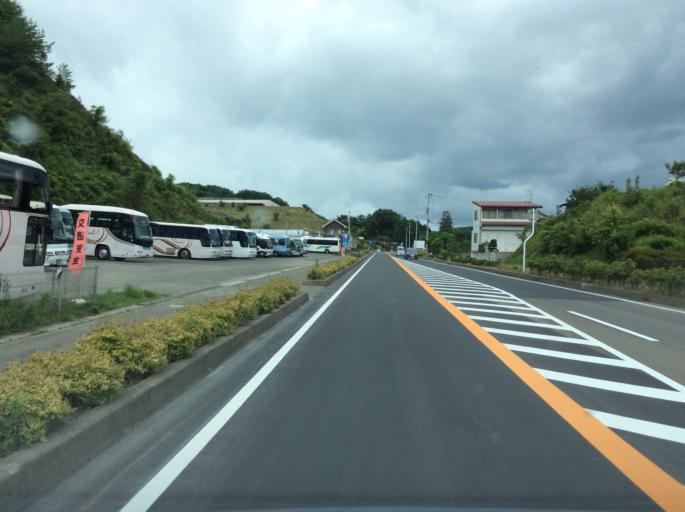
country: JP
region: Fukushima
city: Fukushima-shi
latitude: 37.6629
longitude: 140.5948
